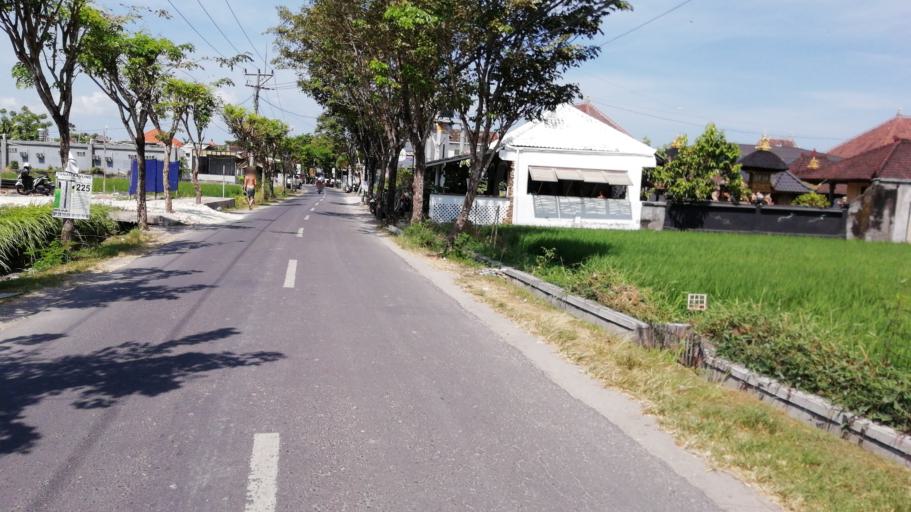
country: ID
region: Bali
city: Banjar Kerobokan
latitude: -8.6602
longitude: 115.1397
